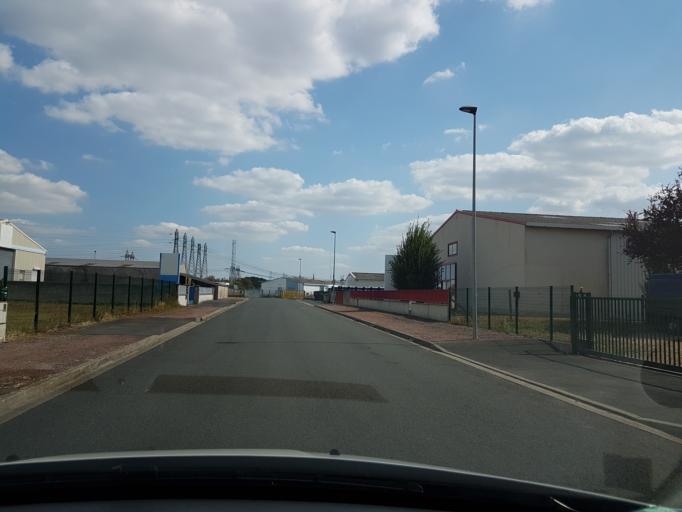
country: FR
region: Centre
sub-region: Departement d'Indre-et-Loire
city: Larcay
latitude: 47.3543
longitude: 0.7643
